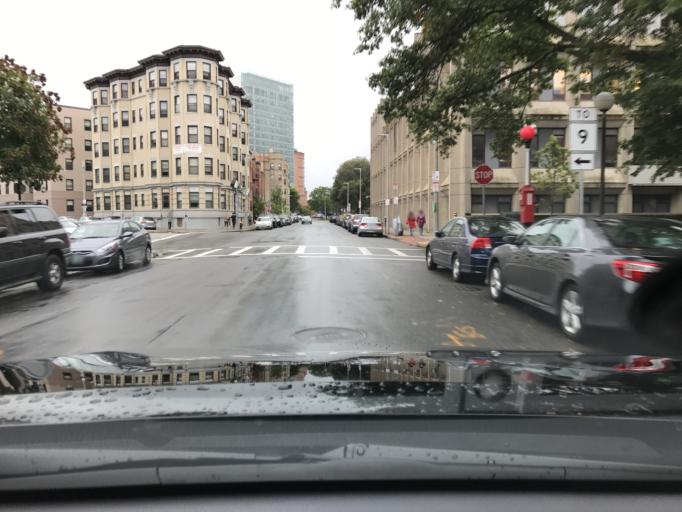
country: US
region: Massachusetts
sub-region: Norfolk County
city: Brookline
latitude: 42.3412
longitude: -71.0911
